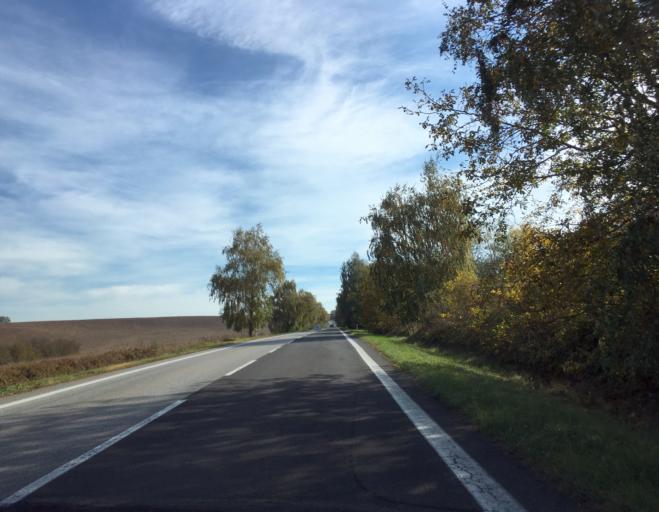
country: SK
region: Nitriansky
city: Zeliezovce
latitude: 48.1268
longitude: 18.7127
